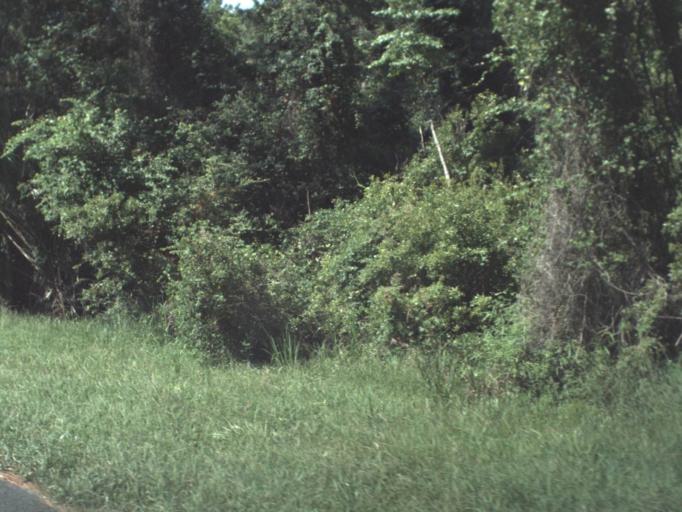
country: US
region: Florida
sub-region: Duval County
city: Atlantic Beach
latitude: 30.4857
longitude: -81.4400
